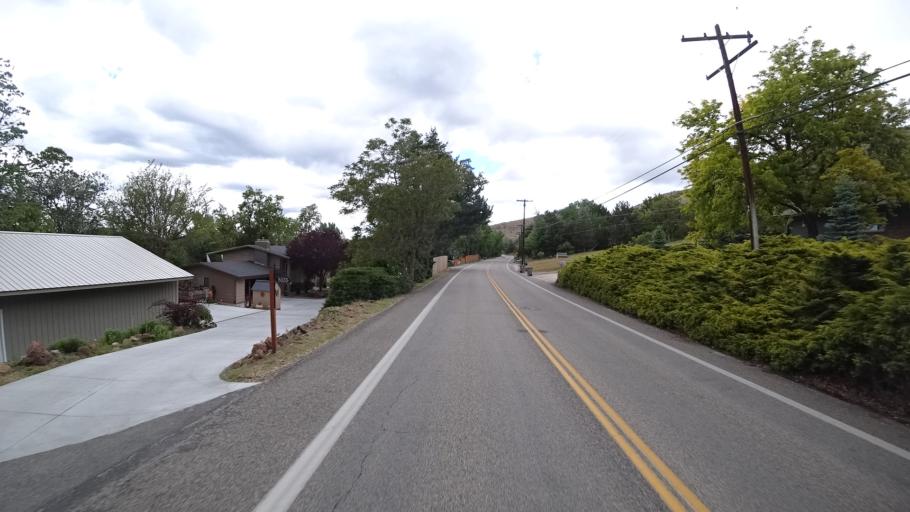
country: US
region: Idaho
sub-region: Ada County
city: Garden City
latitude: 43.6699
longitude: -116.2548
